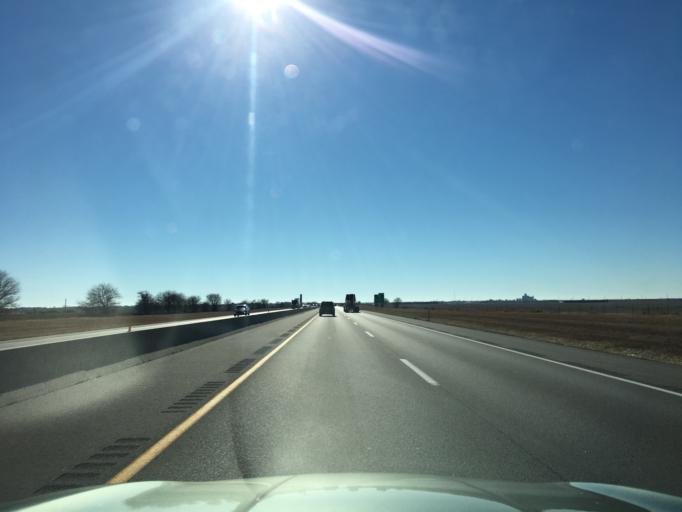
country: US
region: Kansas
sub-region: Sumner County
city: Wellington
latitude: 37.3006
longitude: -97.3404
